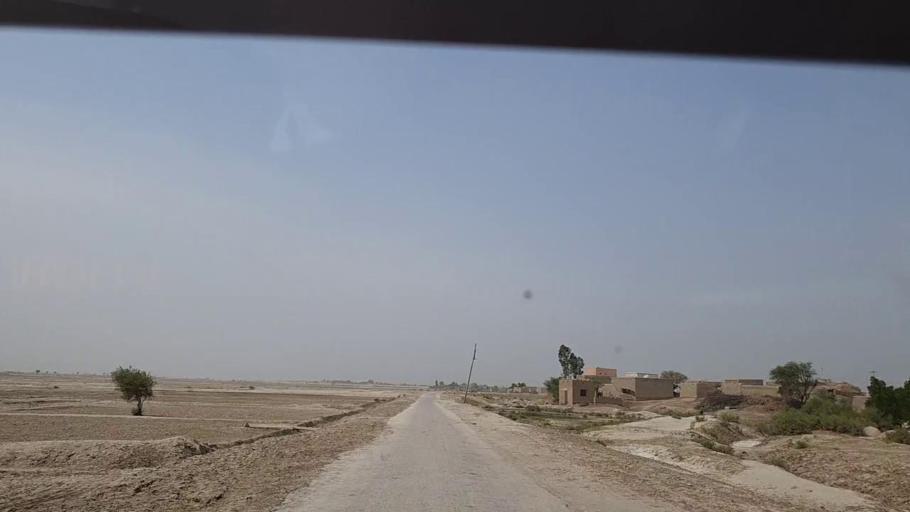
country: PK
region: Sindh
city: Khairpur Nathan Shah
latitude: 27.0629
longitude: 67.6484
